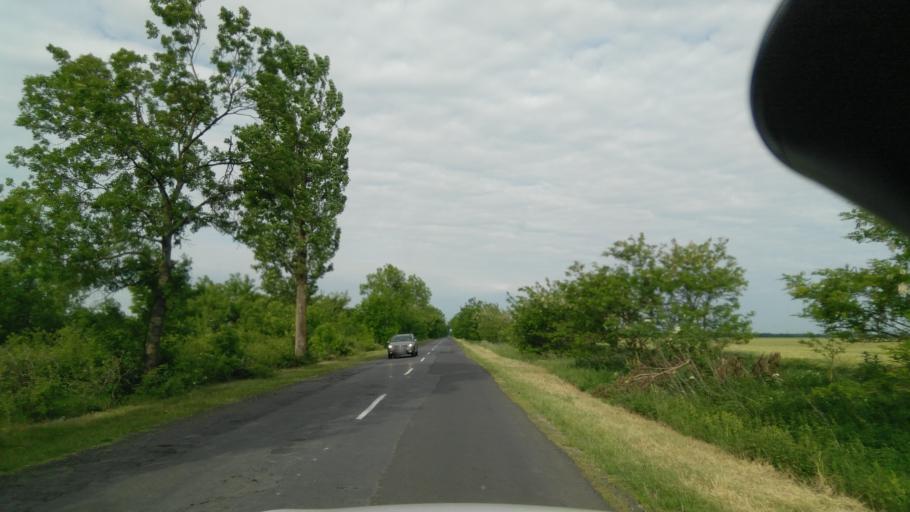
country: HU
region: Bekes
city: Ketegyhaza
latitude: 46.5347
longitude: 21.1252
